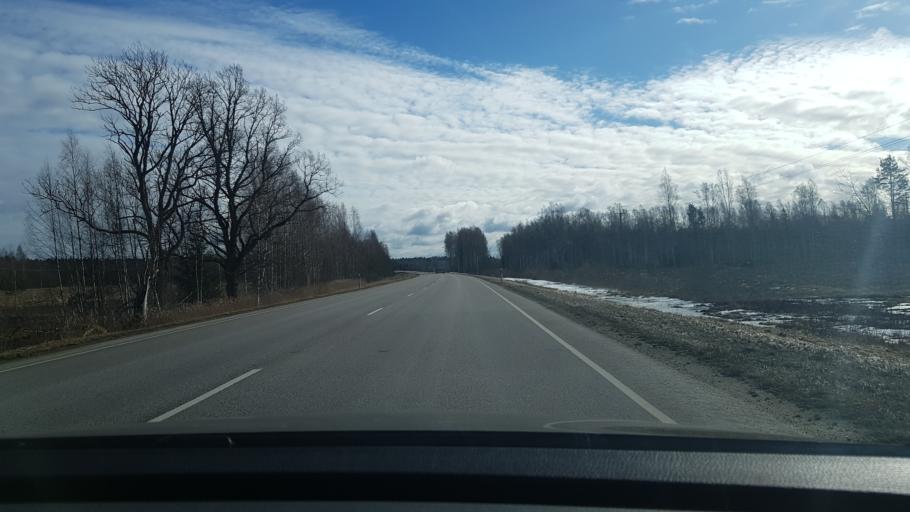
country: EE
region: Paernumaa
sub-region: Saarde vald
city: Kilingi-Nomme
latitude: 58.1757
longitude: 24.8047
